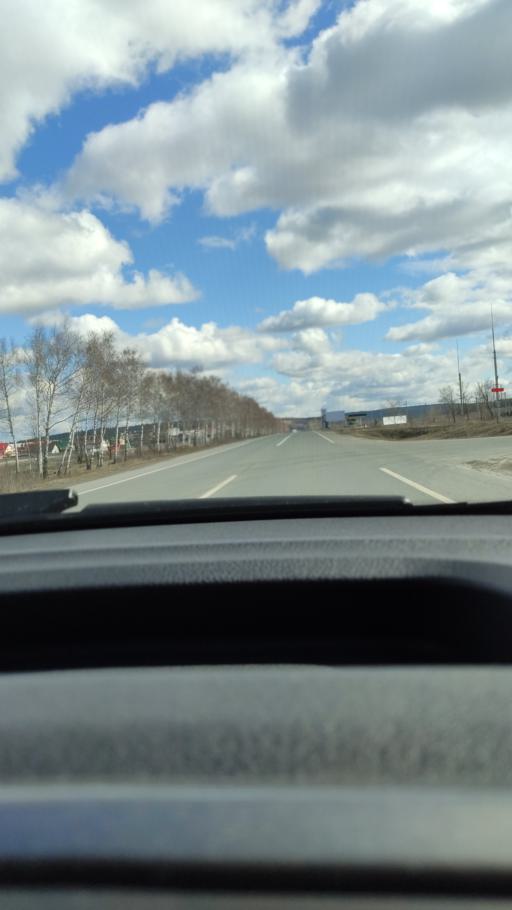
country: RU
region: Samara
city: Kurumoch
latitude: 53.4866
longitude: 50.0105
